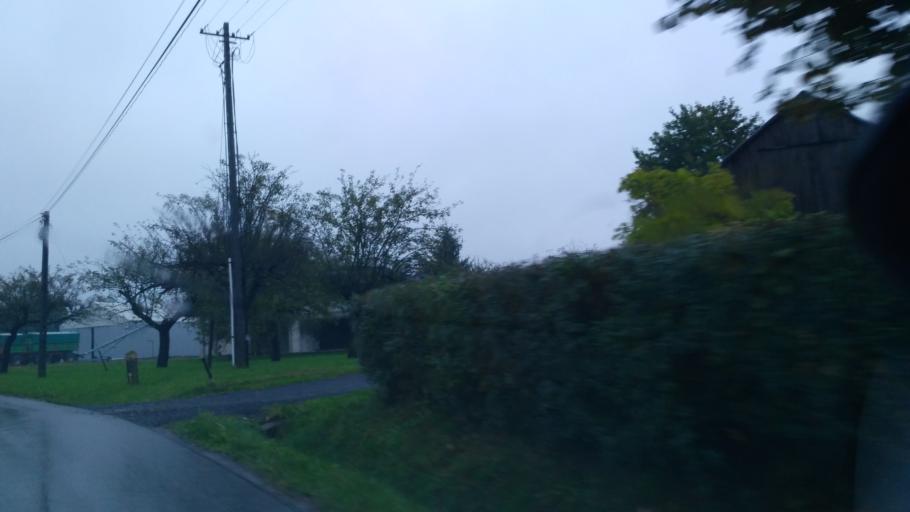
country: PL
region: Subcarpathian Voivodeship
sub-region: Powiat krosnienski
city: Korczyna
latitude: 49.7107
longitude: 21.8131
